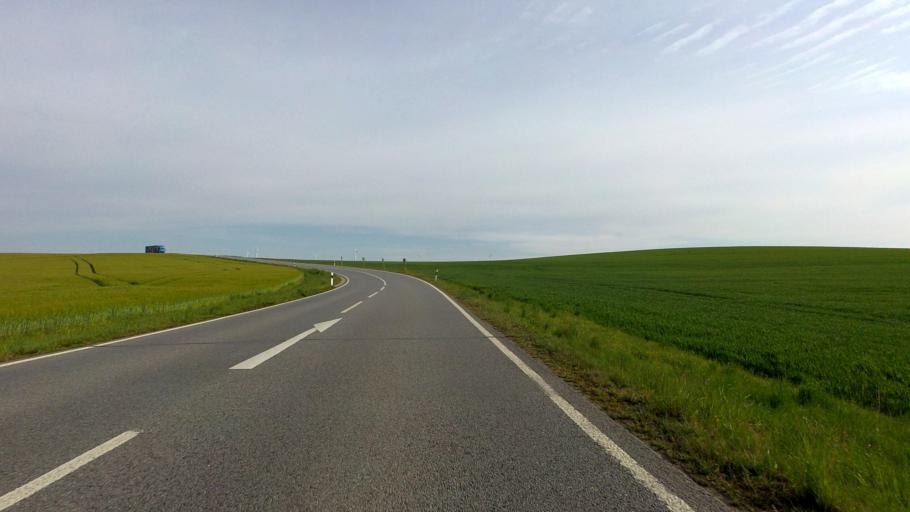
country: DE
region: Saxony
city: Stolpen
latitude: 51.0610
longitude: 14.0592
